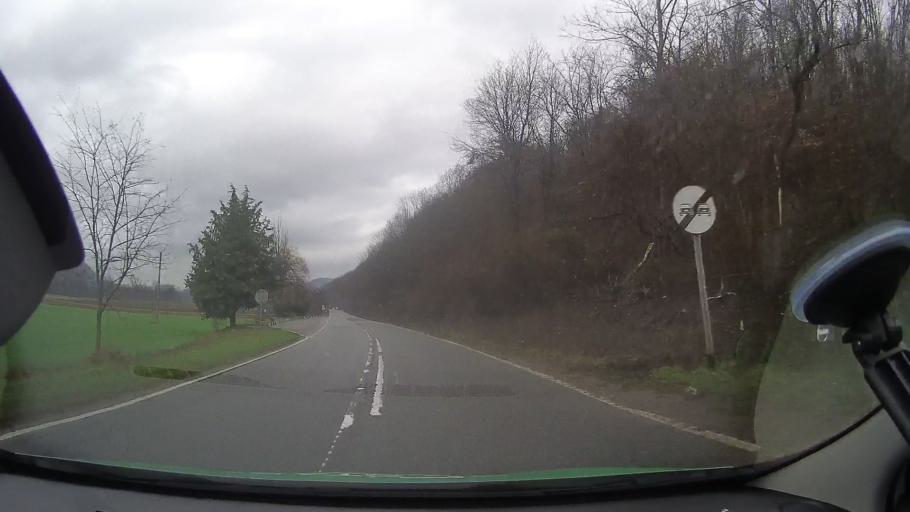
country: RO
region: Arad
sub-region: Comuna Buteni
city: Buteni
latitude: 46.3060
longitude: 22.1525
